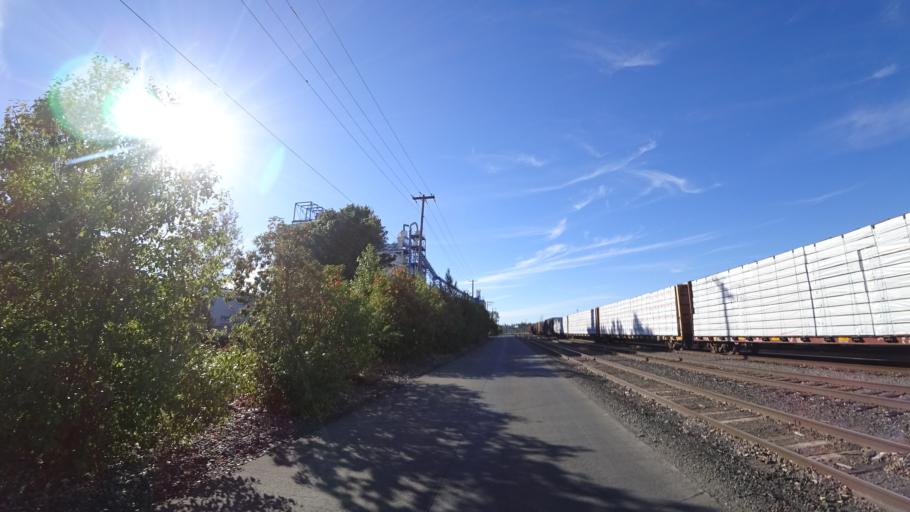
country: US
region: Oregon
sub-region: Multnomah County
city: Portland
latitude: 45.5487
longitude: -122.6921
